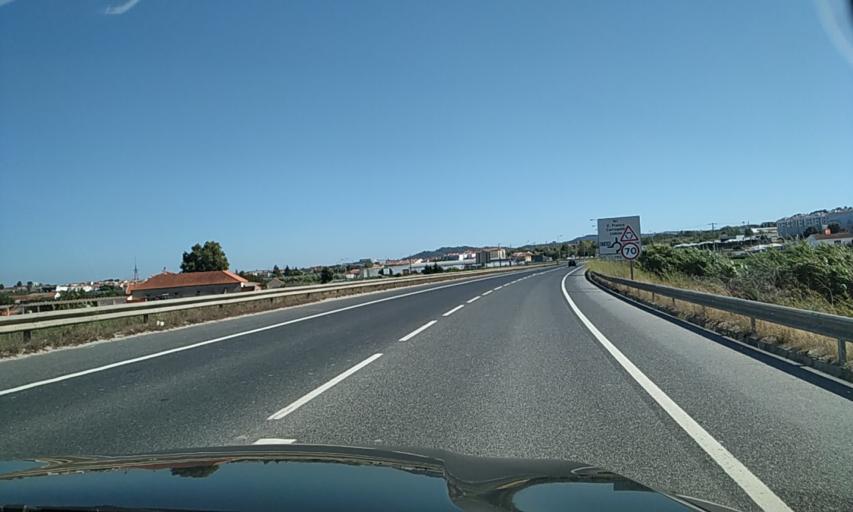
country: PT
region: Lisbon
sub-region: Alenquer
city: Alenquer
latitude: 39.0529
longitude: -8.9943
